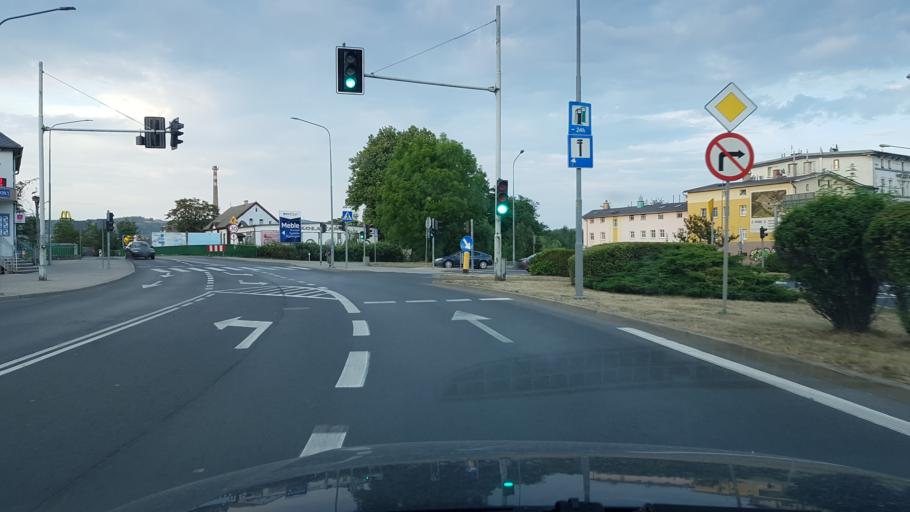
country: PL
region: Lower Silesian Voivodeship
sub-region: Jelenia Gora
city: Jelenia Gora
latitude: 50.9056
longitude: 15.7351
